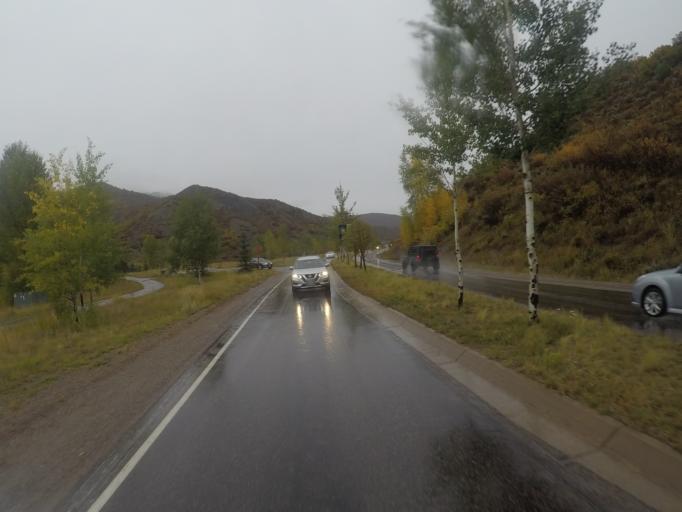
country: US
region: Colorado
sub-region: Pitkin County
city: Snowmass Village
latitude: 39.2257
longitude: -106.9200
